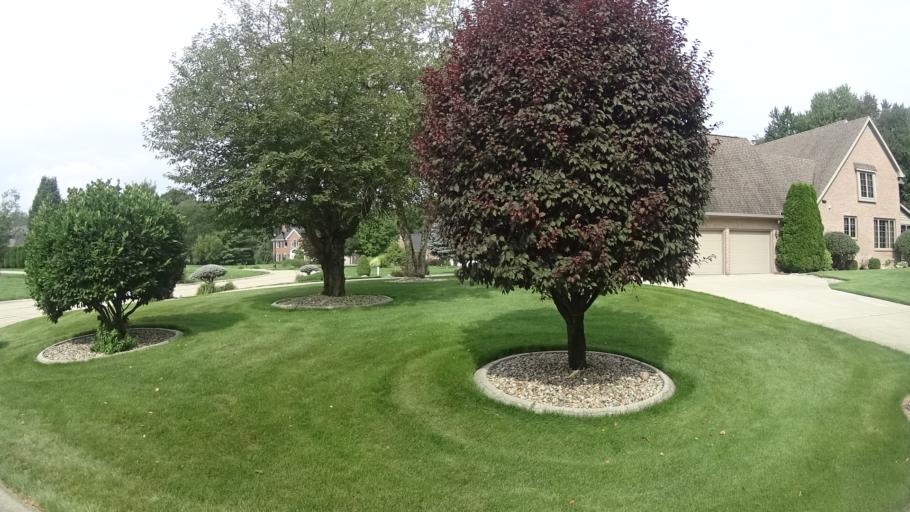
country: US
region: Indiana
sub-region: Madison County
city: Pendleton
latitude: 40.0154
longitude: -85.7871
